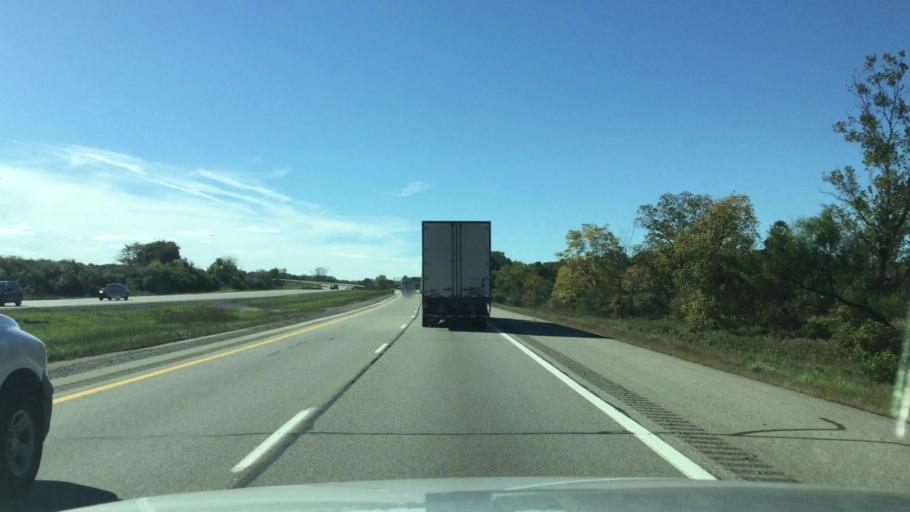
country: US
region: Michigan
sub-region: Washtenaw County
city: Ann Arbor
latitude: 42.3252
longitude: -83.6793
